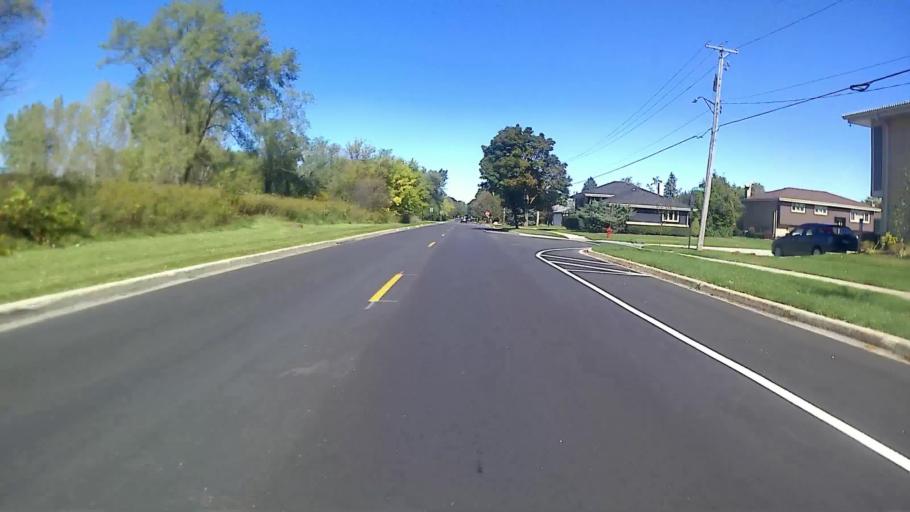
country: US
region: Illinois
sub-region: DuPage County
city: Itasca
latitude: 41.9587
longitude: -88.0033
